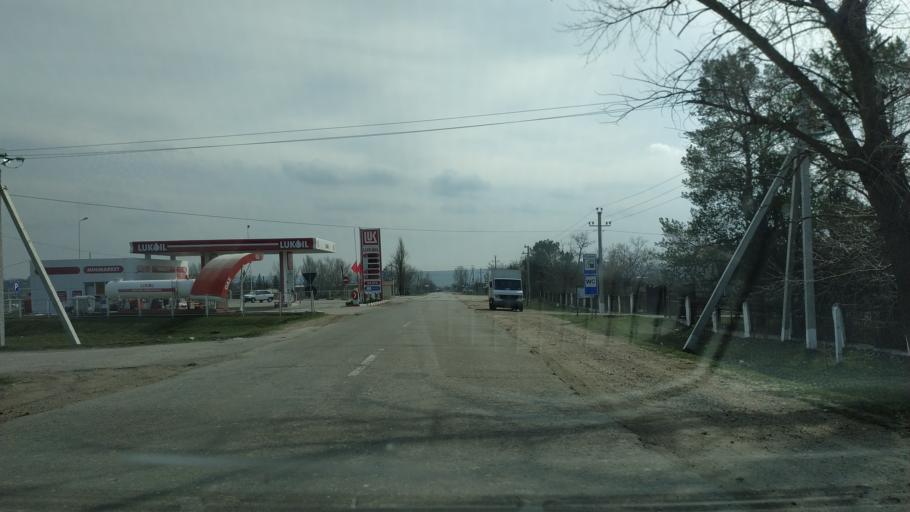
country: MD
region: Gagauzia
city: Vulcanesti
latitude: 45.6991
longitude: 28.4029
